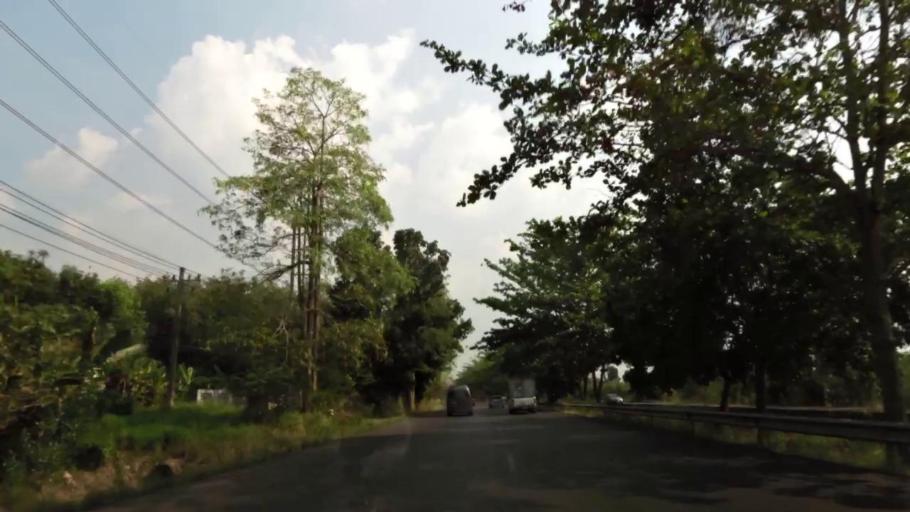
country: TH
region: Rayong
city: Wang Chan
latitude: 12.8854
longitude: 101.5552
